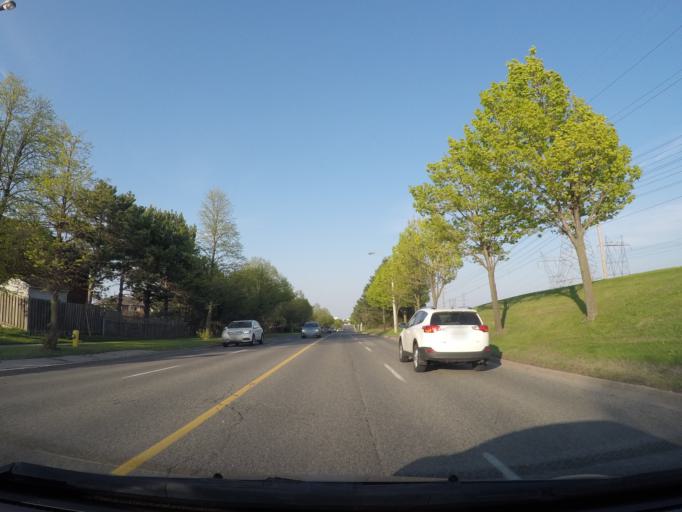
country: CA
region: Ontario
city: Scarborough
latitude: 43.8185
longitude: -79.2693
